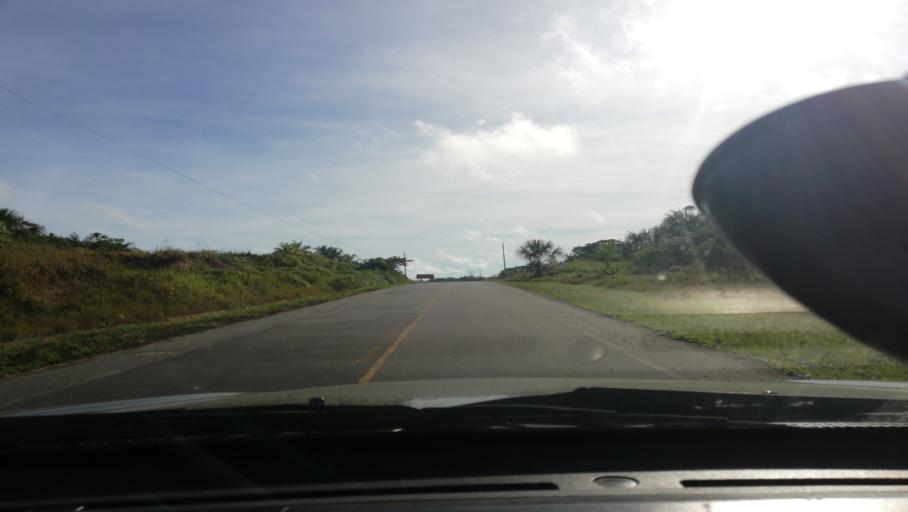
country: PE
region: Loreto
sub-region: Provincia de Loreto
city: Nauta
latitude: -4.3474
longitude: -73.5429
